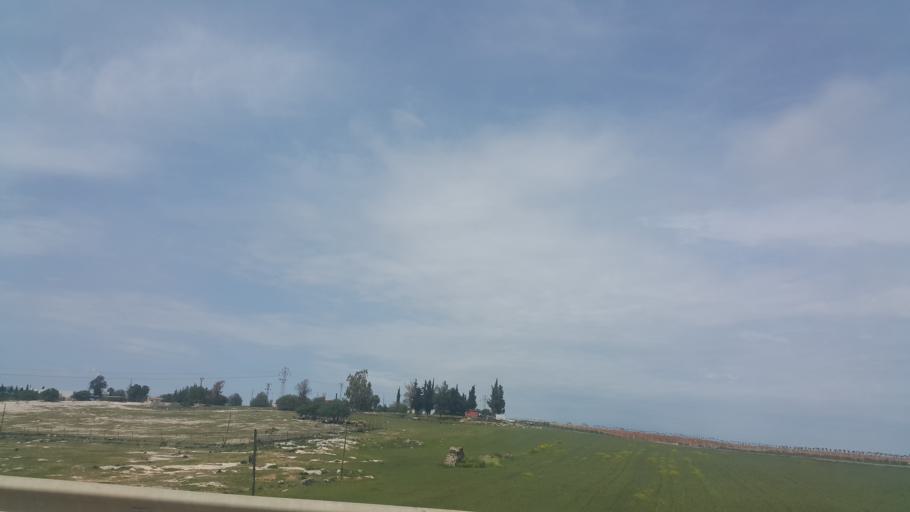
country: TR
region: Adana
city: Yakapinar
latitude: 36.9669
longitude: 35.6307
